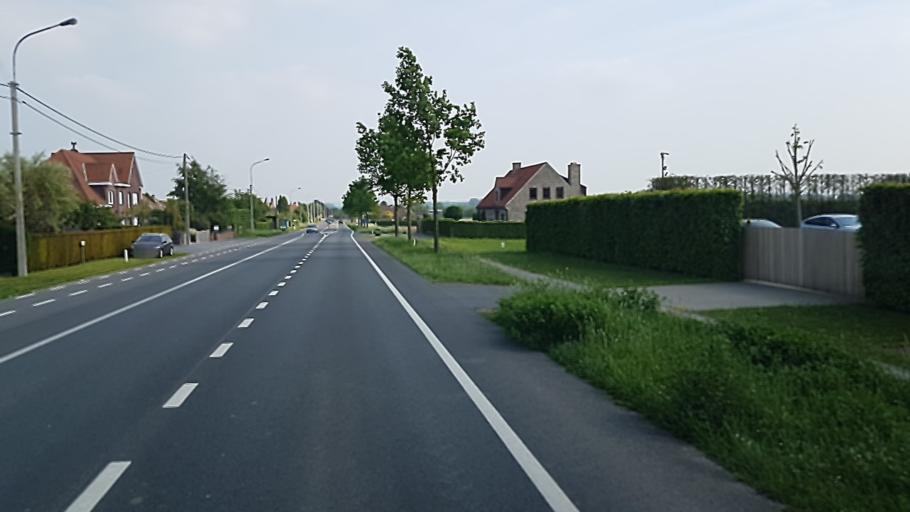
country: BE
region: Wallonia
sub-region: Province du Hainaut
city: Pecq
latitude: 50.7419
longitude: 3.3249
